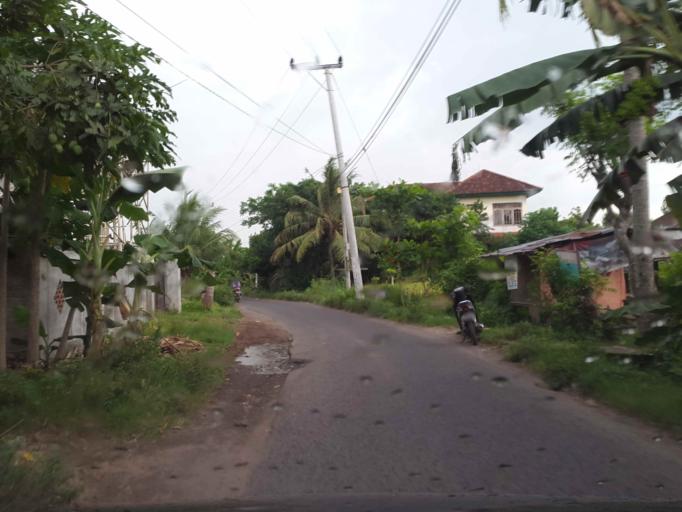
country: ID
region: West Nusa Tenggara
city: Kekeri
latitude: -8.5565
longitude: 116.1183
